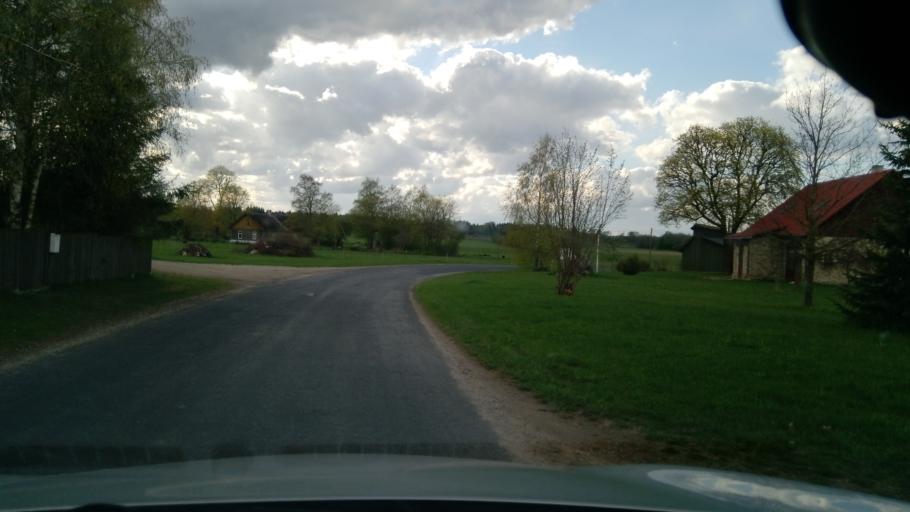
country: EE
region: Jaervamaa
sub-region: Jaerva-Jaani vald
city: Jarva-Jaani
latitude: 59.0121
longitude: 25.7378
